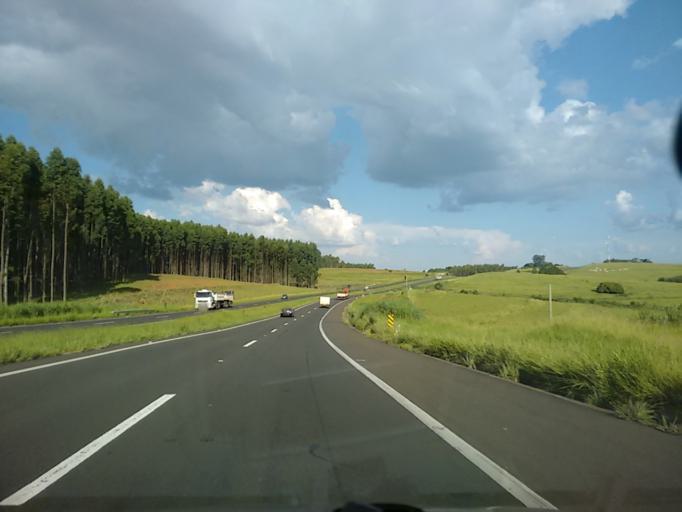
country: BR
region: Sao Paulo
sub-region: Duartina
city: Duartina
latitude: -22.3244
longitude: -49.3981
